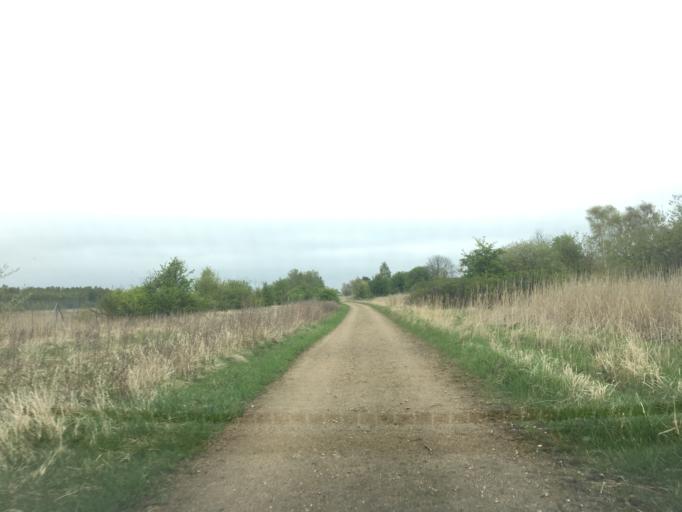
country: DK
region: Capital Region
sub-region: Tarnby Kommune
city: Tarnby
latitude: 55.5885
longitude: 12.5695
